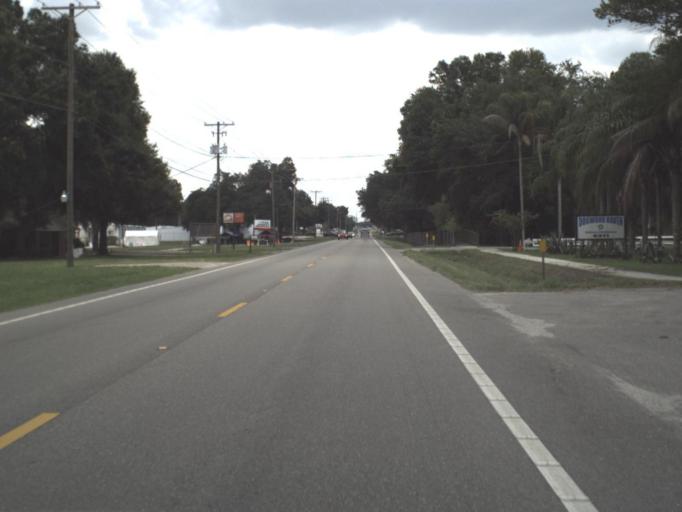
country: US
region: Florida
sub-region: Hillsborough County
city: Dover
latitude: 28.0202
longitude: -82.1713
